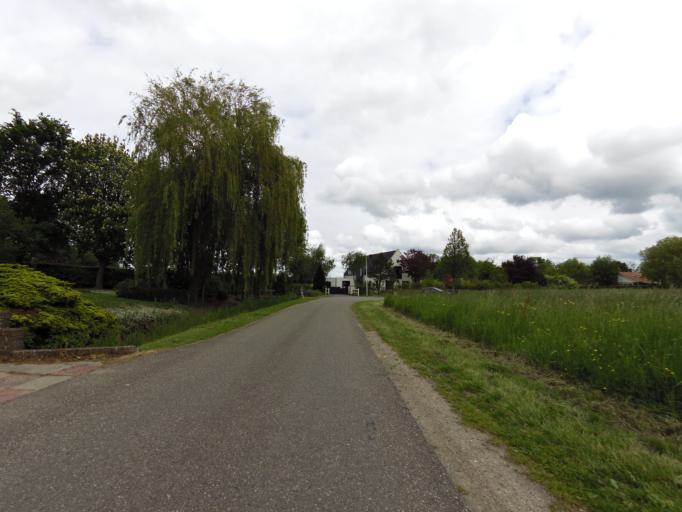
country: NL
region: South Holland
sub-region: Gemeente Brielle
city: Brielle
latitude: 51.9015
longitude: 4.1062
